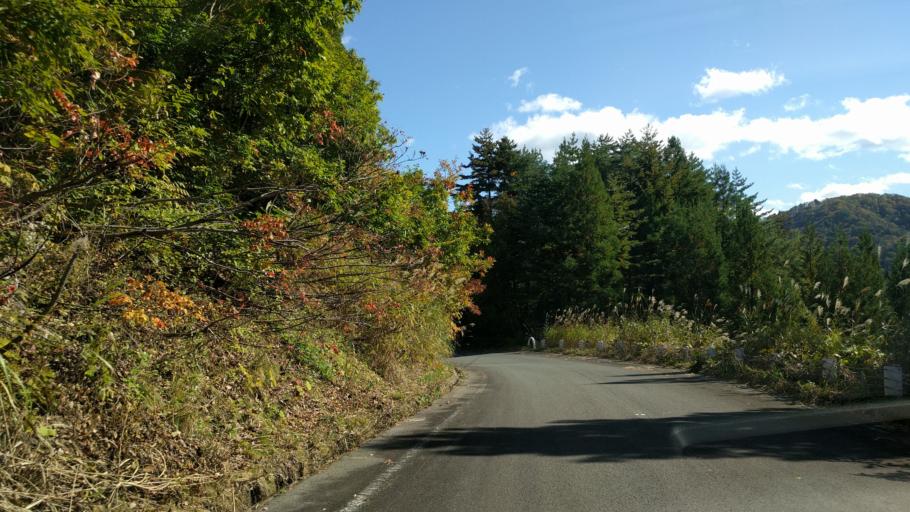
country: JP
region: Fukushima
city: Kitakata
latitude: 37.4216
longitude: 139.7789
